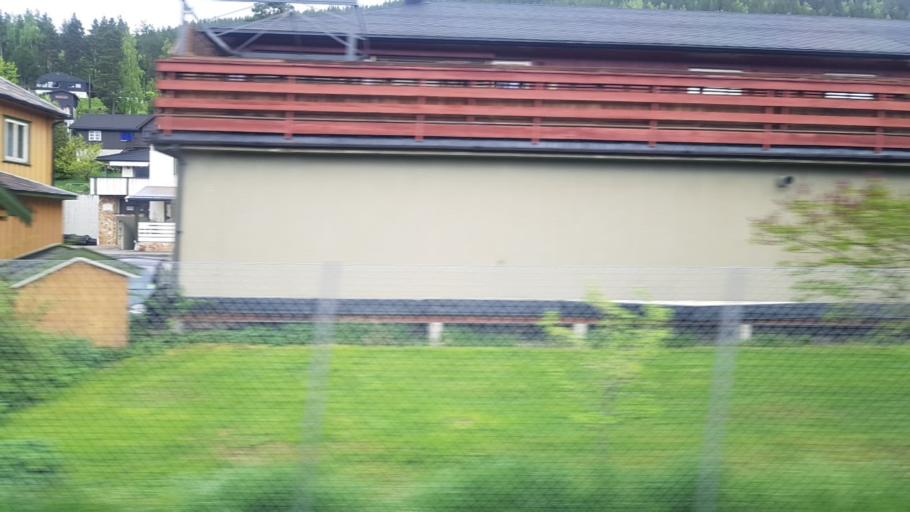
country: NO
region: Oppland
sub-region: Nord-Fron
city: Vinstra
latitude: 61.5945
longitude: 9.7359
